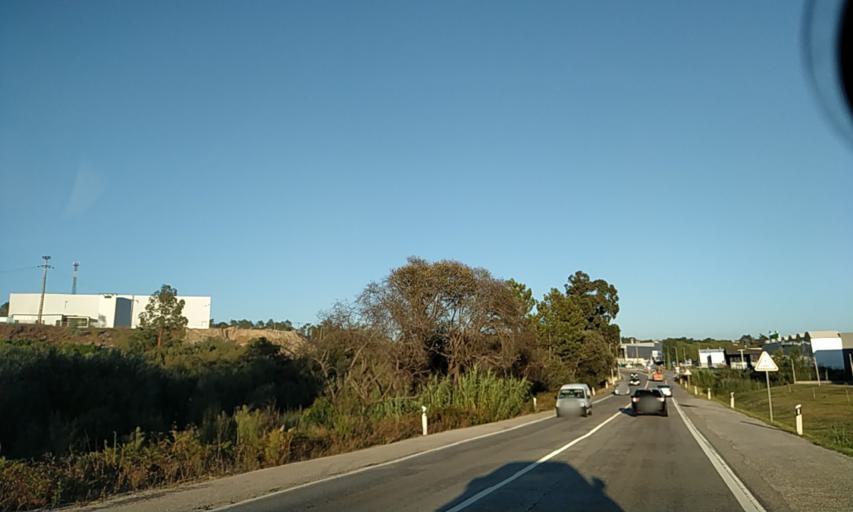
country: PT
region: Aveiro
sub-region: Oliveira do Bairro
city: Oia
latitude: 40.5573
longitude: -8.5581
